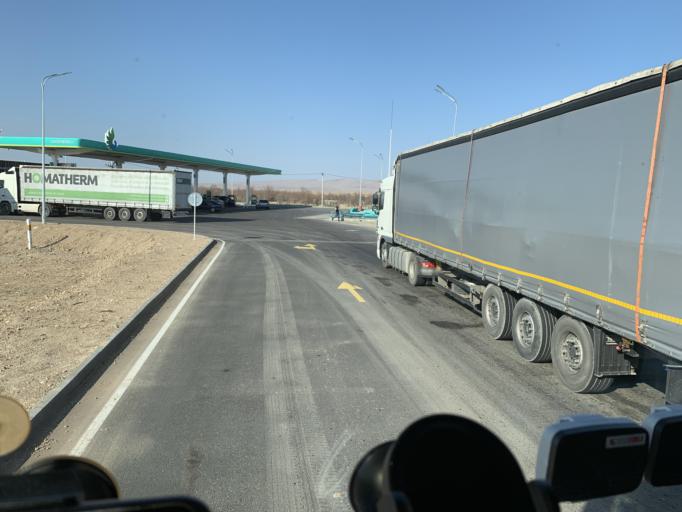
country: KZ
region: Zhambyl
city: Taraz
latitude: 42.8201
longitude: 71.1547
